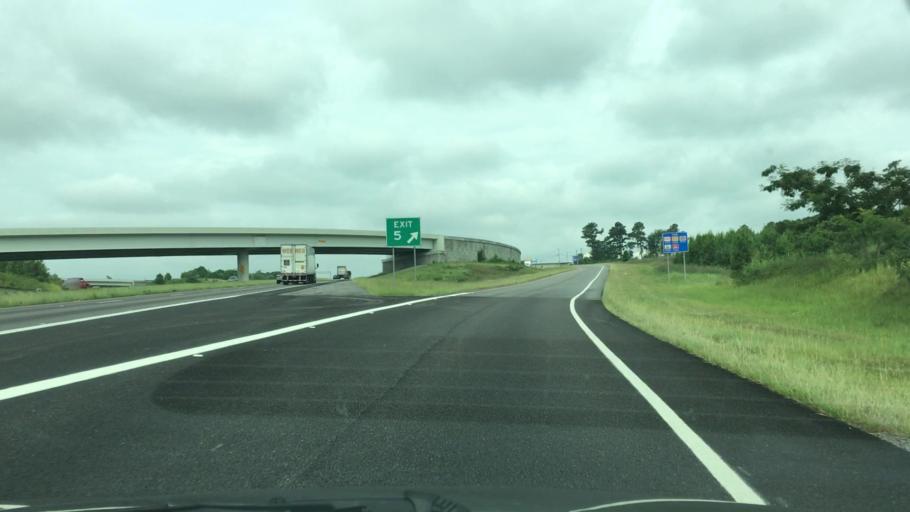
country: US
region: South Carolina
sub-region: Edgefield County
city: Murphys Estates
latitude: 33.5679
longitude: -81.9264
